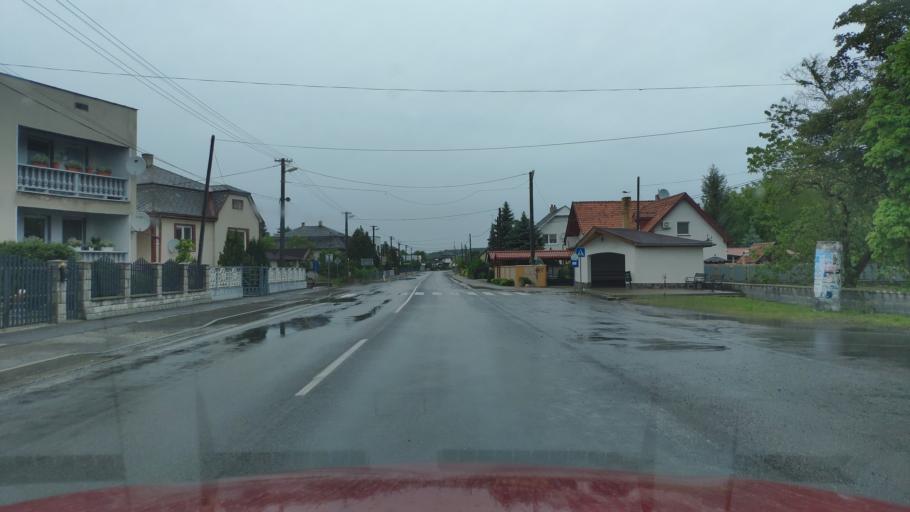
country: HU
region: Borsod-Abauj-Zemplen
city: Ricse
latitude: 48.4323
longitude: 21.9183
